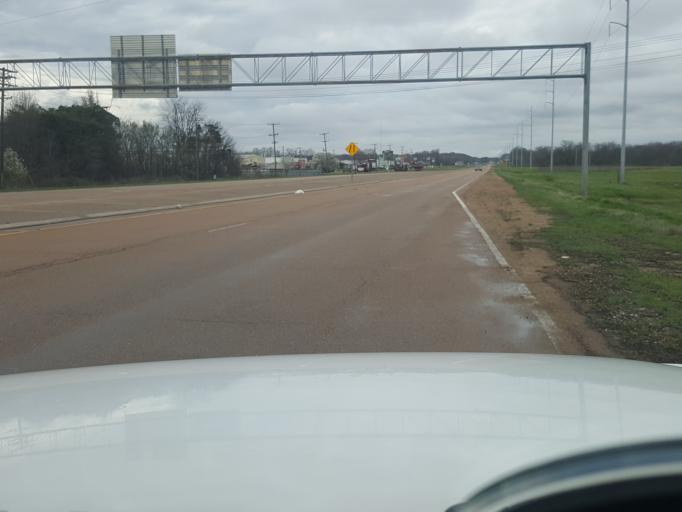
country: US
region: Mississippi
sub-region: Yazoo County
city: Yazoo City
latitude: 32.8568
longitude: -90.4302
